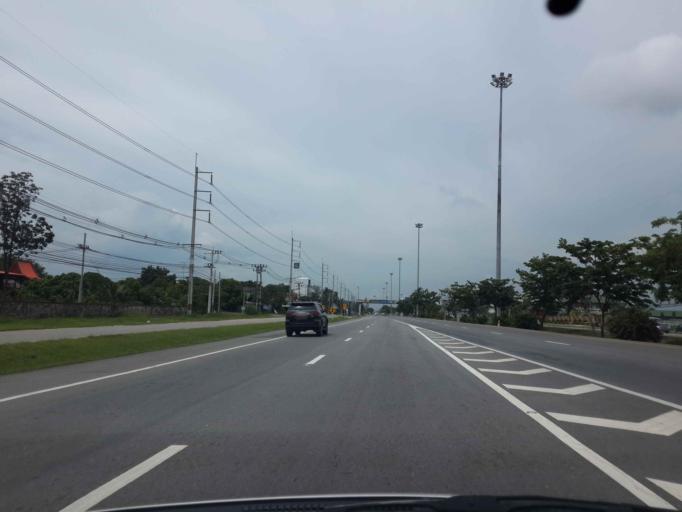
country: TH
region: Ratchaburi
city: Pak Tho
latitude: 13.3436
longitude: 99.8297
